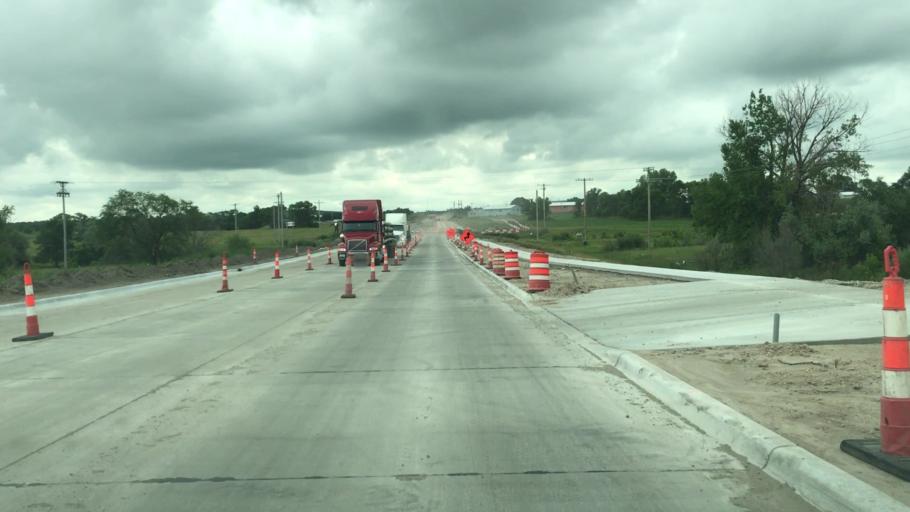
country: US
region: South Dakota
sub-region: Todd County
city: Mission
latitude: 43.3039
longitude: -100.6527
